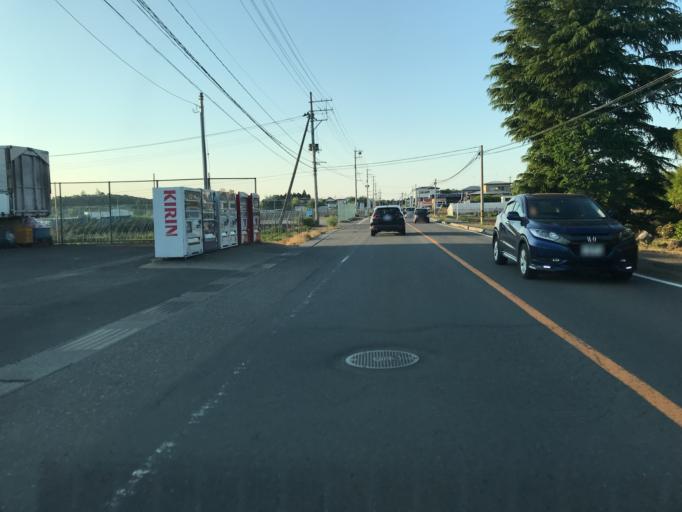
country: JP
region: Fukushima
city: Ishikawa
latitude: 37.1617
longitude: 140.3518
